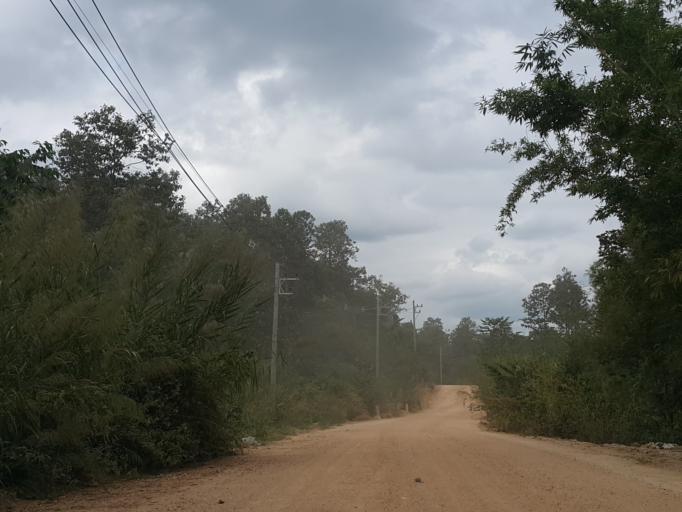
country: TH
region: Lampang
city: Chae Hom
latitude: 18.5776
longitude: 99.4482
